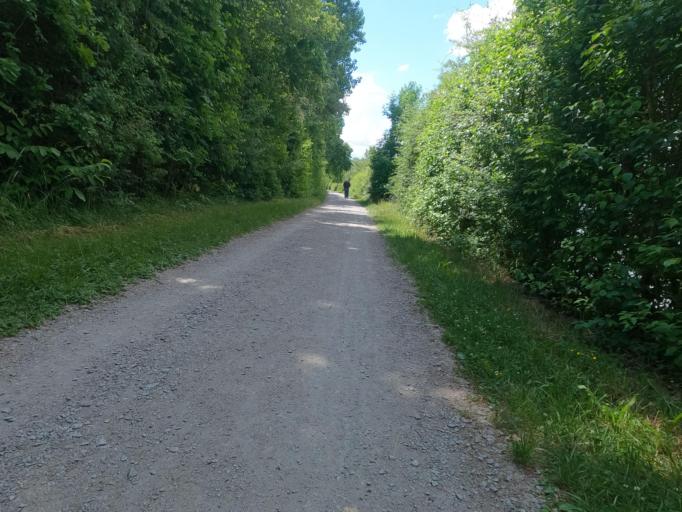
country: DE
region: Hesse
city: Gernsheim
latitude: 49.7439
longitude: 8.4612
